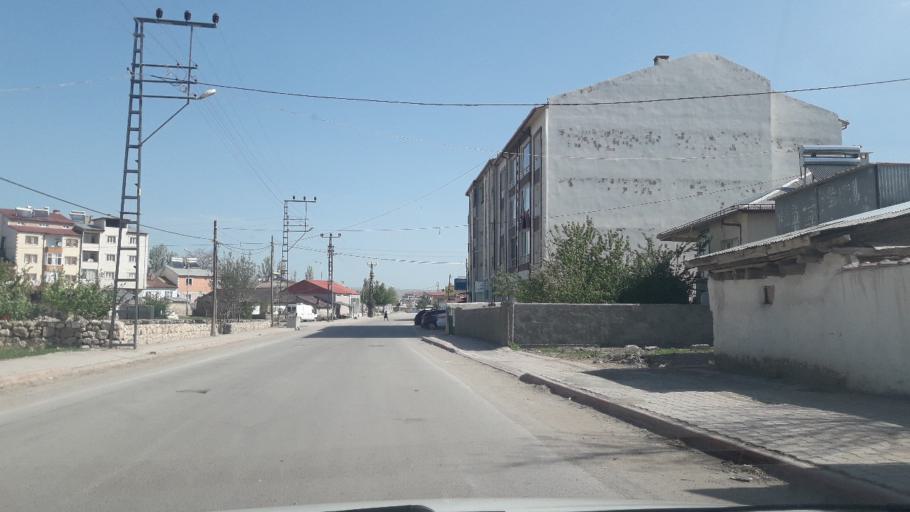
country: TR
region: Sivas
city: Kangal
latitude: 39.2303
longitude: 37.3885
